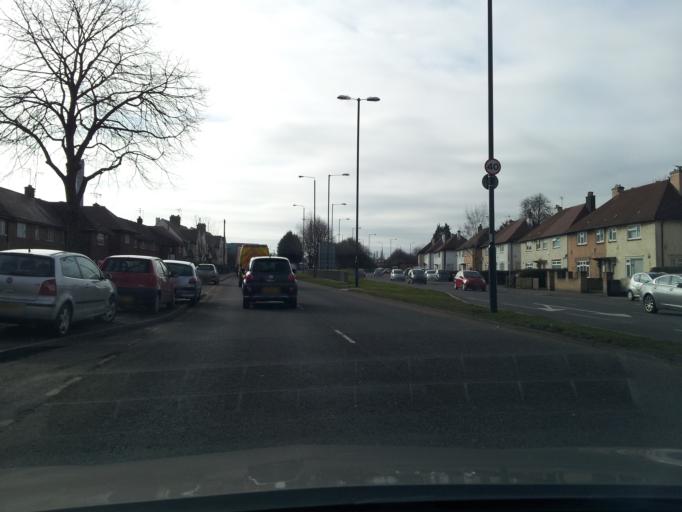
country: GB
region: England
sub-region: Derby
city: Derby
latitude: 52.9133
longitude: -1.5109
